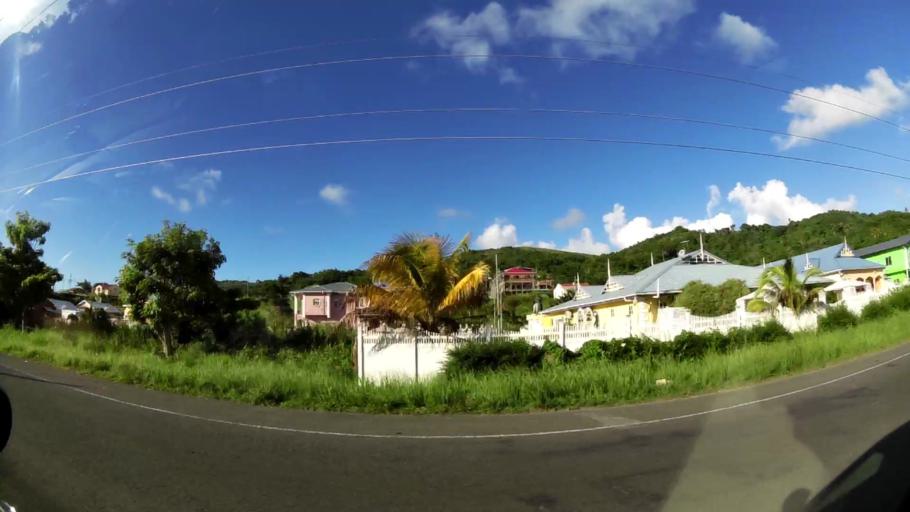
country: TT
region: Tobago
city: Scarborough
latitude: 11.1796
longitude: -60.7097
